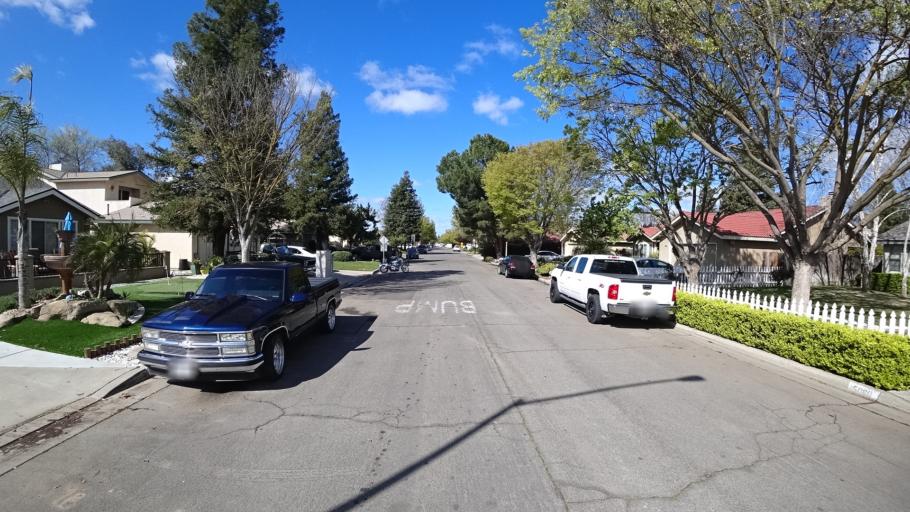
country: US
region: California
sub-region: Fresno County
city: West Park
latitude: 36.8320
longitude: -119.8821
